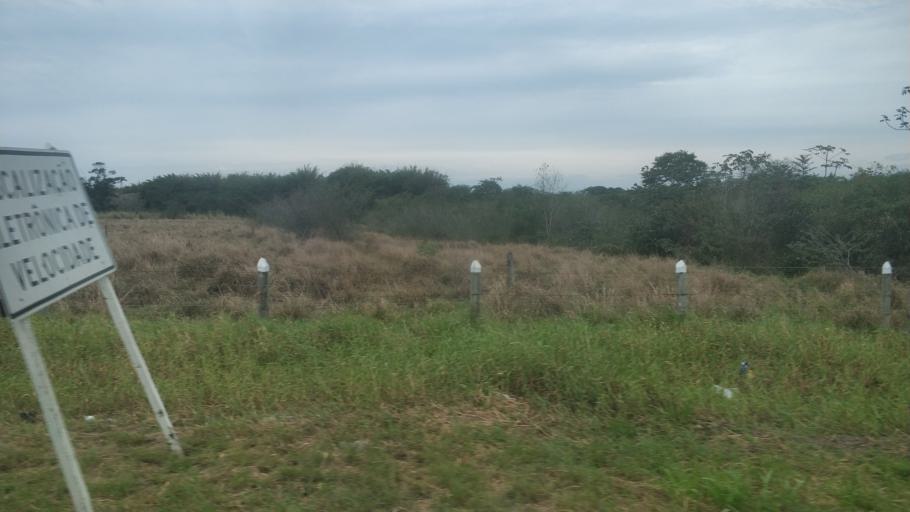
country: BR
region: Rio de Janeiro
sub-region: Seropedica
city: Seropedica
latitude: -22.7723
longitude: -43.6698
